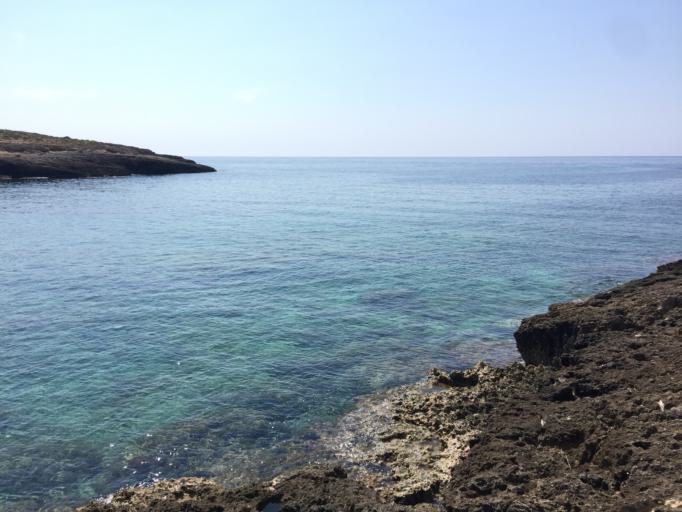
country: IT
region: Sicily
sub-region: Agrigento
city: Lampedusa
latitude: 35.4956
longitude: 12.6124
